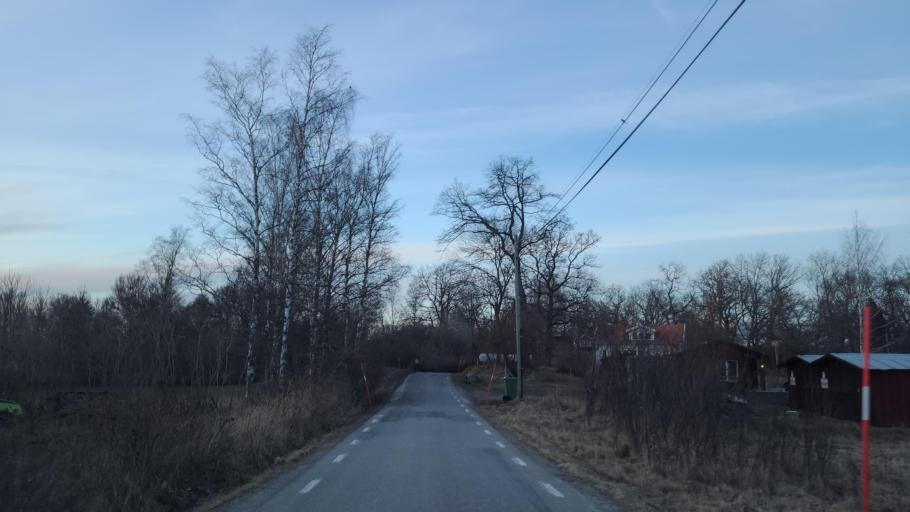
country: SE
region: Stockholm
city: Stenhamra
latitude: 59.4159
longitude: 17.6633
